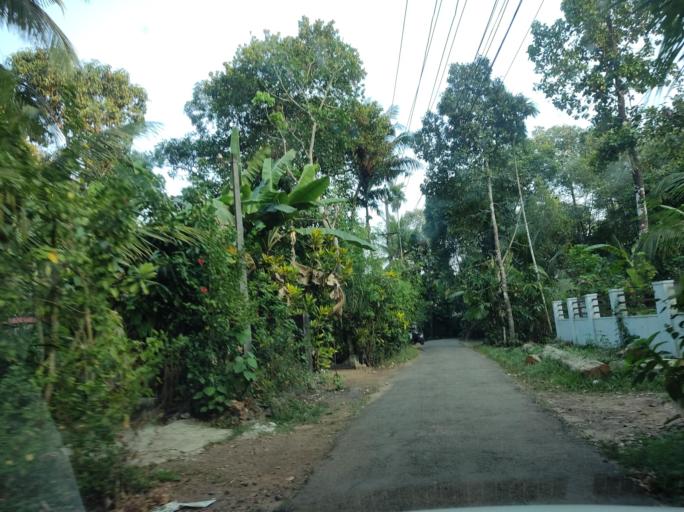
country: IN
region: Kerala
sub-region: Pattanamtitta
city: Tiruvalla
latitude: 9.3654
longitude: 76.5648
